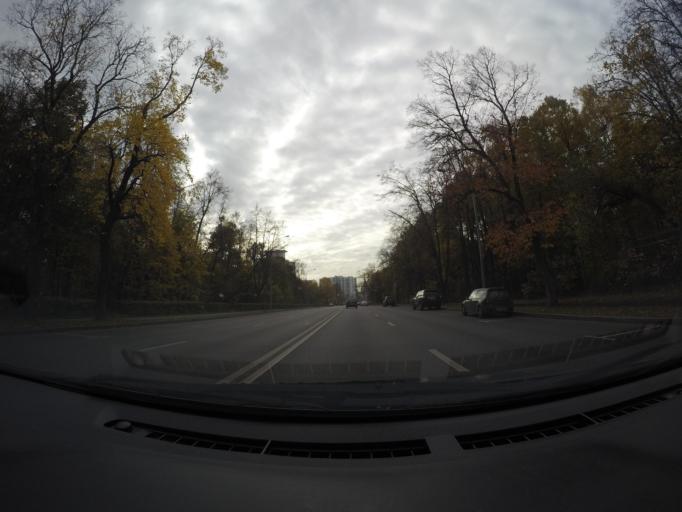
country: RU
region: Moscow
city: Sokol'niki
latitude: 55.7950
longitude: 37.6814
